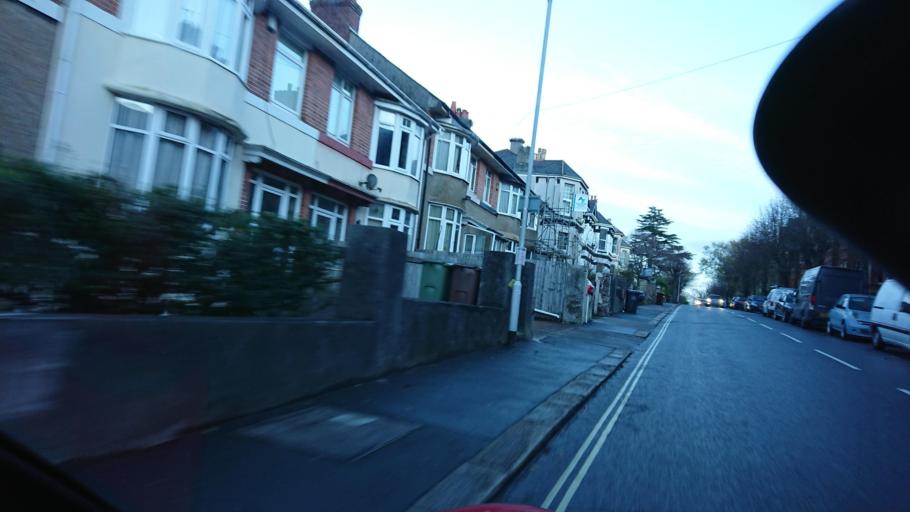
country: GB
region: England
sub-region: Plymouth
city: Plymouth
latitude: 50.3795
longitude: -4.1278
